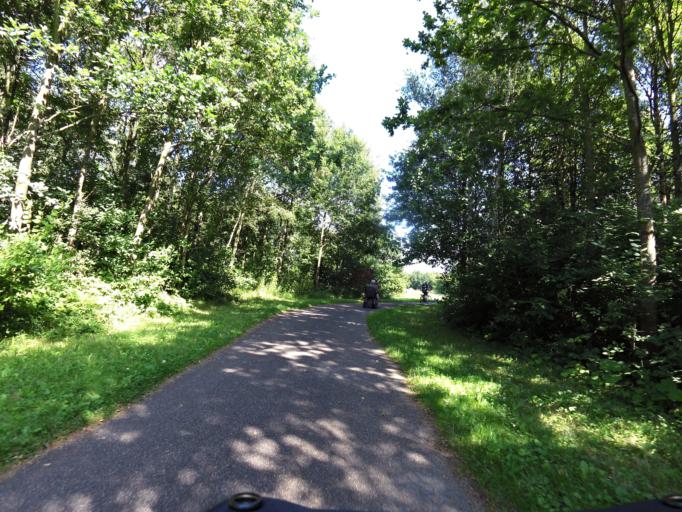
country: NL
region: South Holland
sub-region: Gemeente Barendrecht
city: Barendrecht
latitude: 51.8663
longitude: 4.5256
